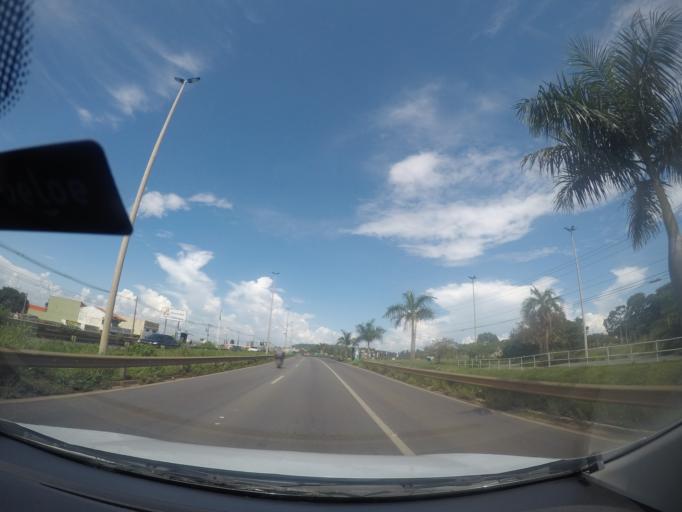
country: BR
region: Goias
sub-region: Goiania
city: Goiania
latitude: -16.6590
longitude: -49.3685
